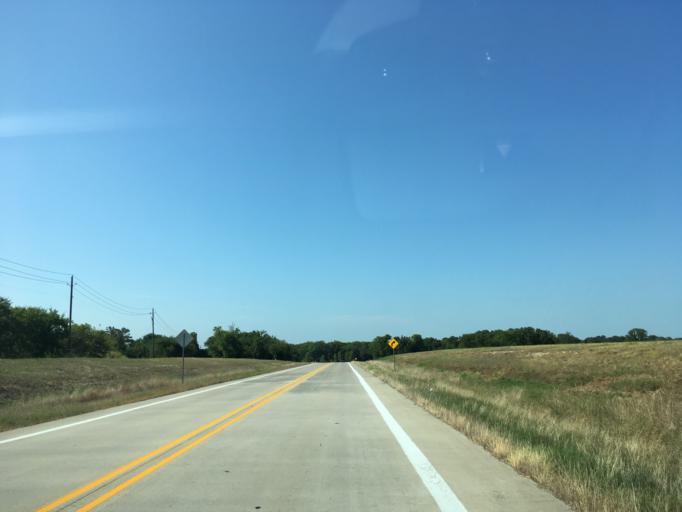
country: US
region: Texas
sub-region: Collin County
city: Lowry Crossing
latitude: 33.1646
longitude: -96.5863
